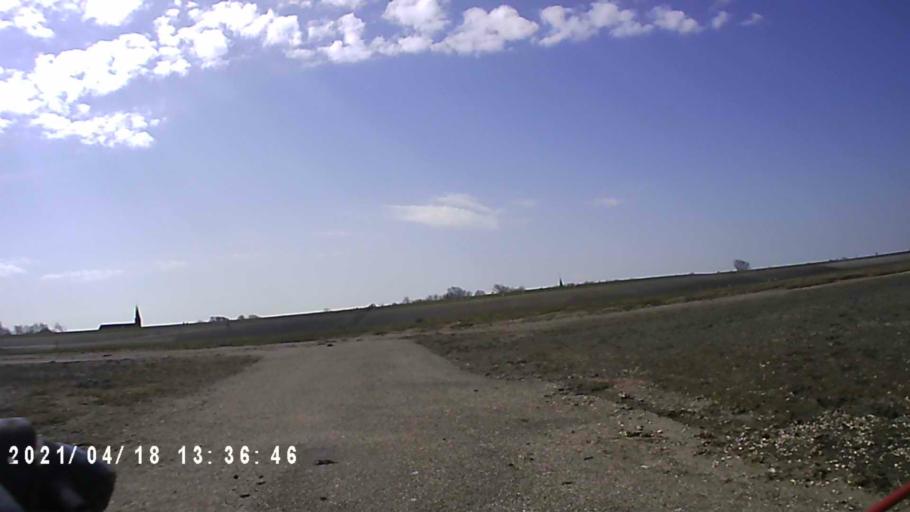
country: NL
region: Friesland
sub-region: Gemeente Dongeradeel
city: Anjum
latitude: 53.4045
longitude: 6.0866
